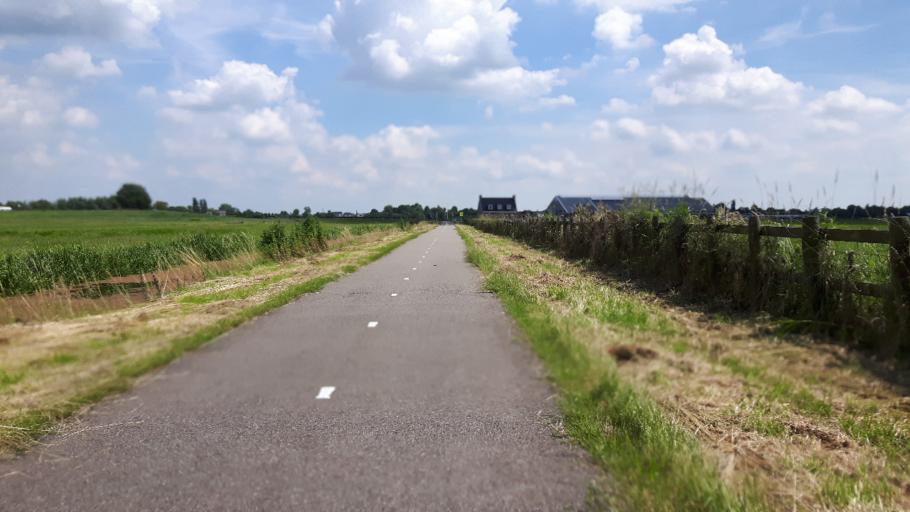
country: NL
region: South Holland
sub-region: Gemeente Boskoop
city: Boskoop
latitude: 52.0740
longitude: 4.6932
